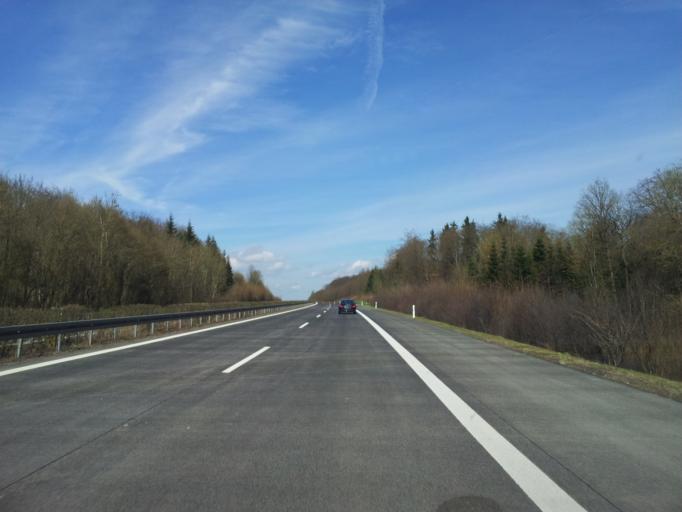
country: DE
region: Baden-Wuerttemberg
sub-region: Regierungsbezirk Stuttgart
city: Buch am Ahorn
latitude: 49.4853
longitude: 9.5658
